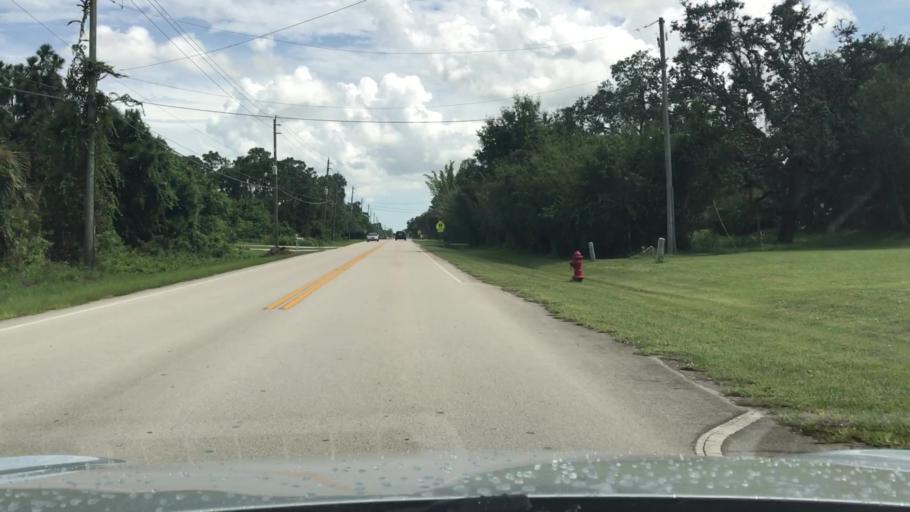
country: US
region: Florida
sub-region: Indian River County
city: Sebastian
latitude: 27.8009
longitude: -80.5019
